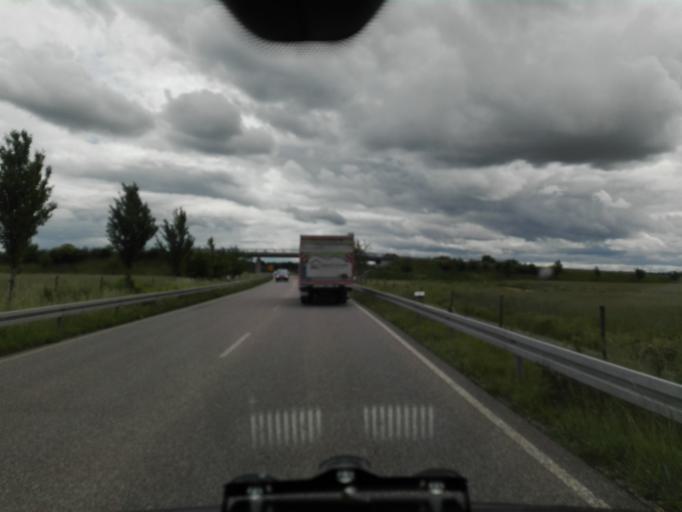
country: DE
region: Baden-Wuerttemberg
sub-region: Karlsruhe Region
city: Graben-Neudorf
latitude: 49.1405
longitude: 8.4686
